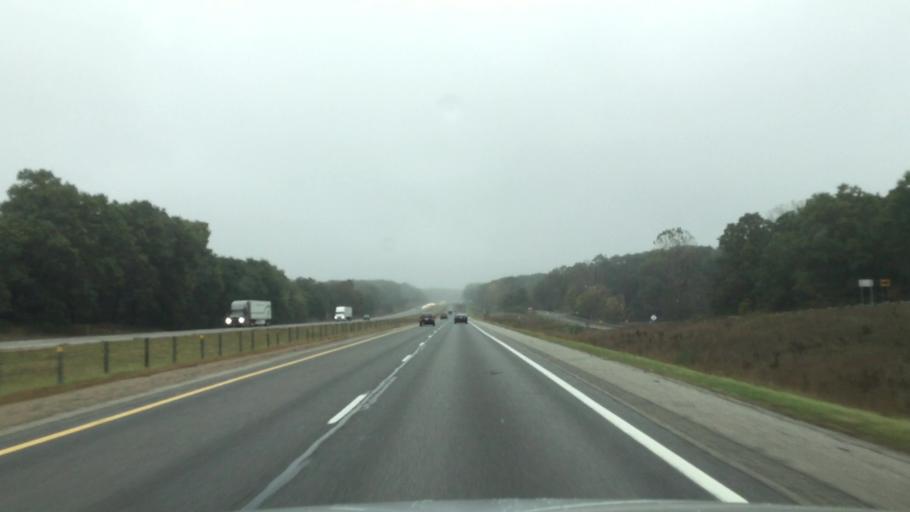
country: US
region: Michigan
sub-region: Van Buren County
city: Mattawan
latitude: 42.2280
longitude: -85.7249
